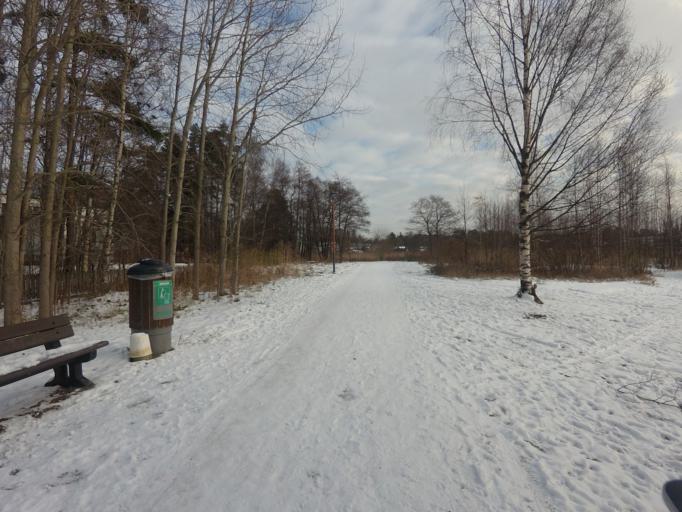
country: FI
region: Uusimaa
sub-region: Helsinki
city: Koukkuniemi
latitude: 60.1496
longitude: 24.7293
